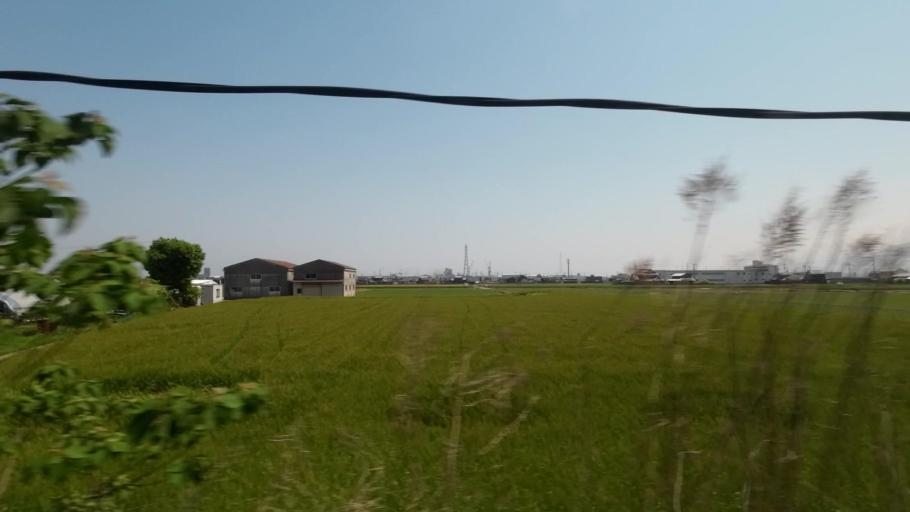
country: JP
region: Ehime
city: Saijo
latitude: 33.9215
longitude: 133.0929
